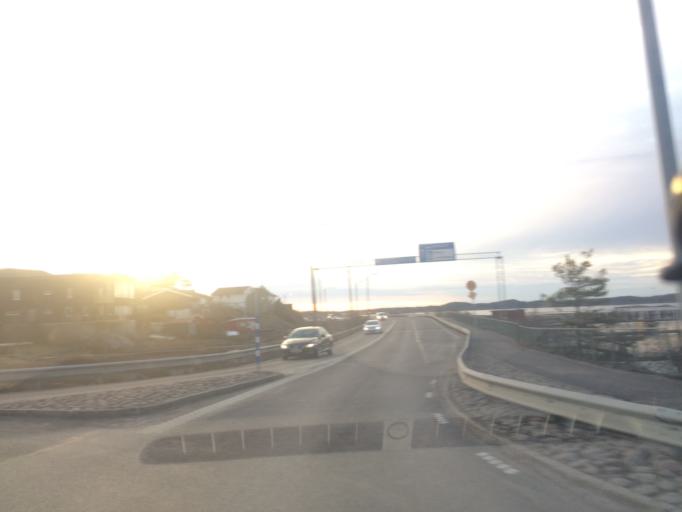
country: SE
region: Vaestra Goetaland
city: Hjuvik
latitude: 57.7110
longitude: 11.7138
